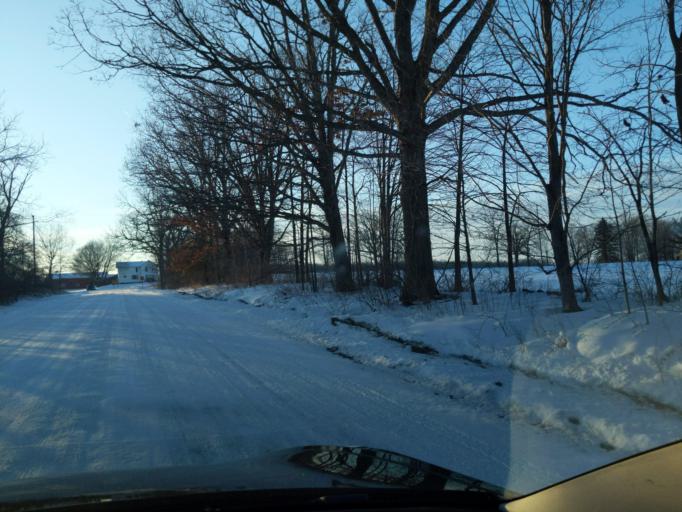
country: US
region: Michigan
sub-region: Ingham County
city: Webberville
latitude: 42.5679
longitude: -84.1413
